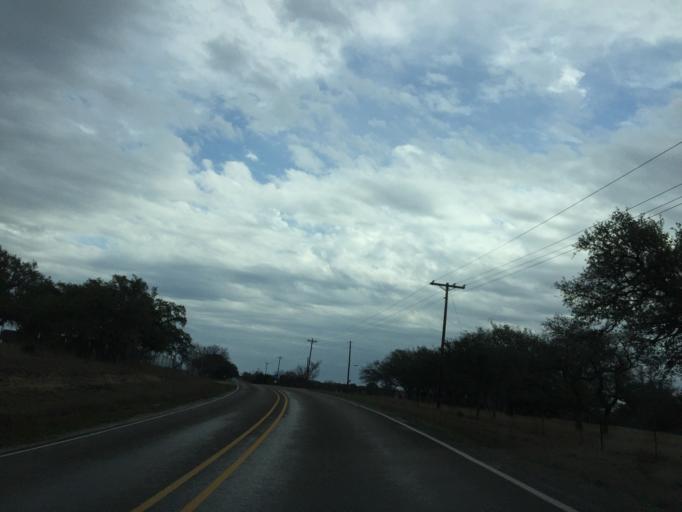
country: US
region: Texas
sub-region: Burnet County
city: Bertram
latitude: 30.6504
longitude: -97.9821
